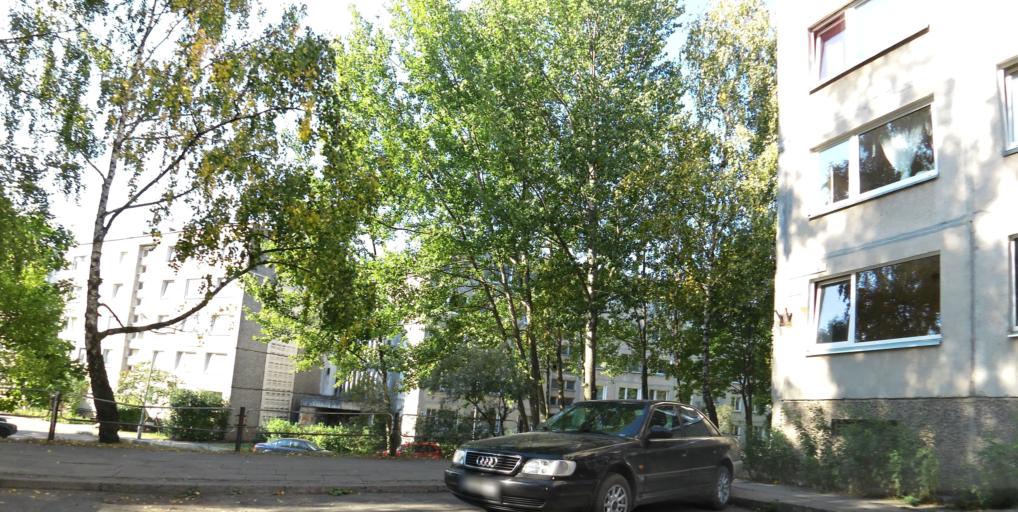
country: LT
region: Vilnius County
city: Justiniskes
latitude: 54.7055
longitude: 25.2225
